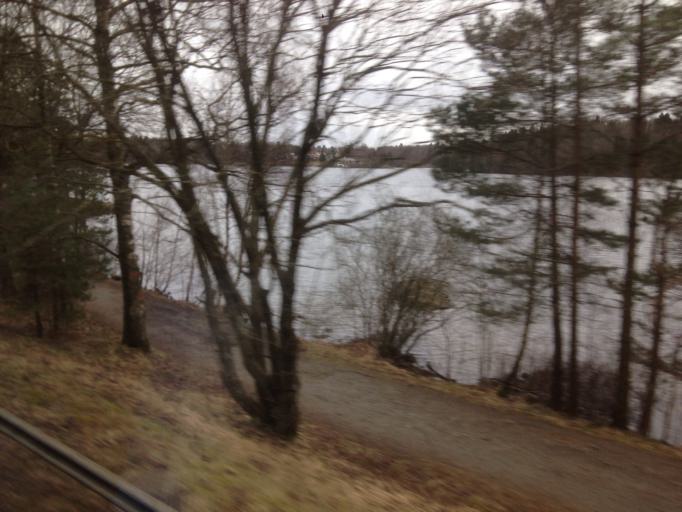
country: SE
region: Vaestra Goetaland
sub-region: Partille Kommun
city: Furulund
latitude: 57.7142
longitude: 12.1412
